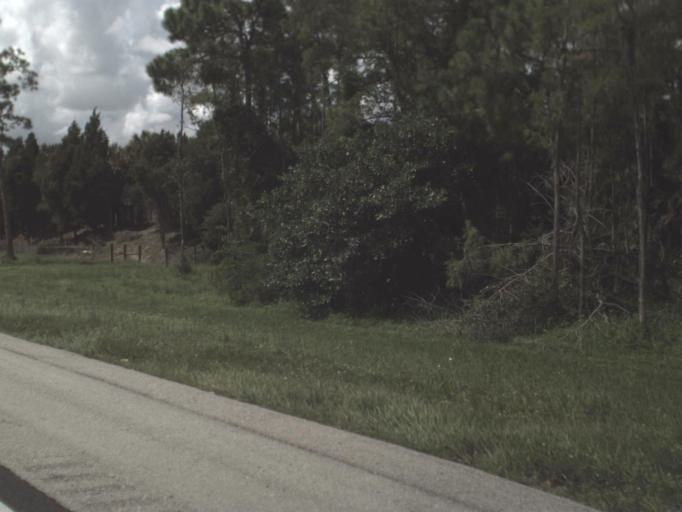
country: US
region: Florida
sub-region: Lee County
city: Bonita Springs
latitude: 26.2862
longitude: -81.7430
